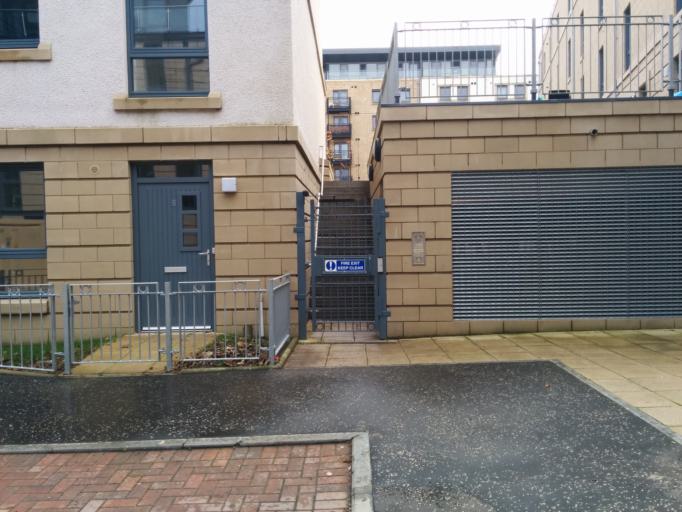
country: GB
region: Scotland
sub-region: Edinburgh
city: Colinton
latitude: 55.9354
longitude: -3.2368
